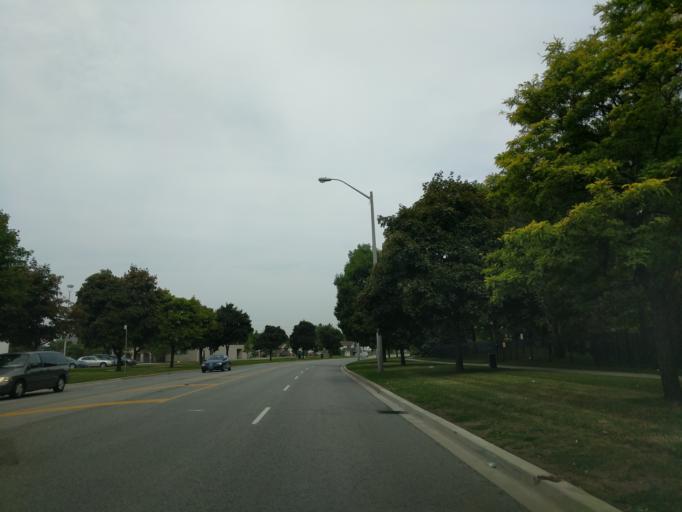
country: CA
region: Ontario
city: Scarborough
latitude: 43.7998
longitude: -79.3175
